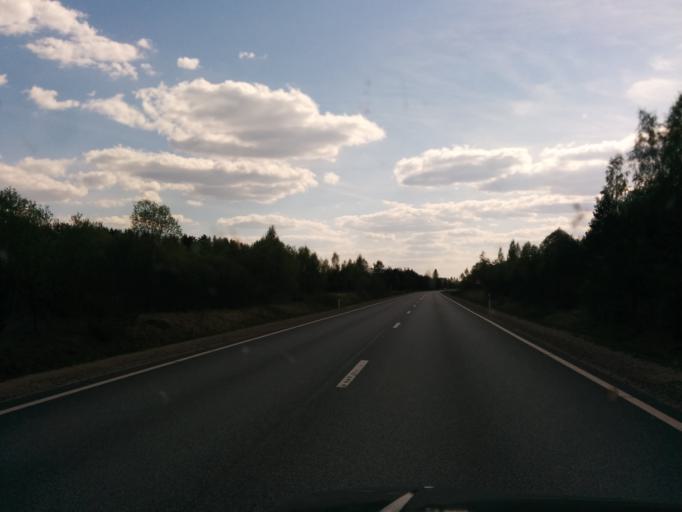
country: LV
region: Krimulda
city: Ragana
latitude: 57.2138
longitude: 24.7841
